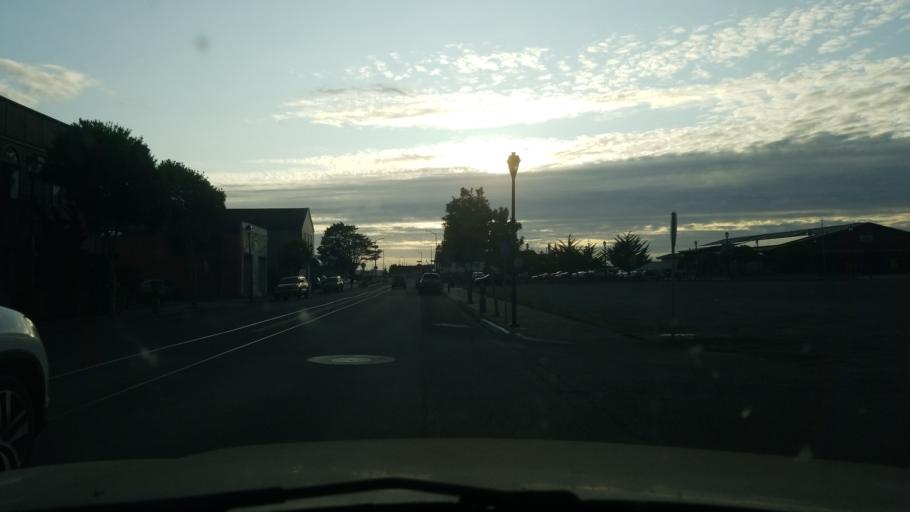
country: US
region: California
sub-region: Humboldt County
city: Eureka
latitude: 40.8050
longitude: -124.1688
